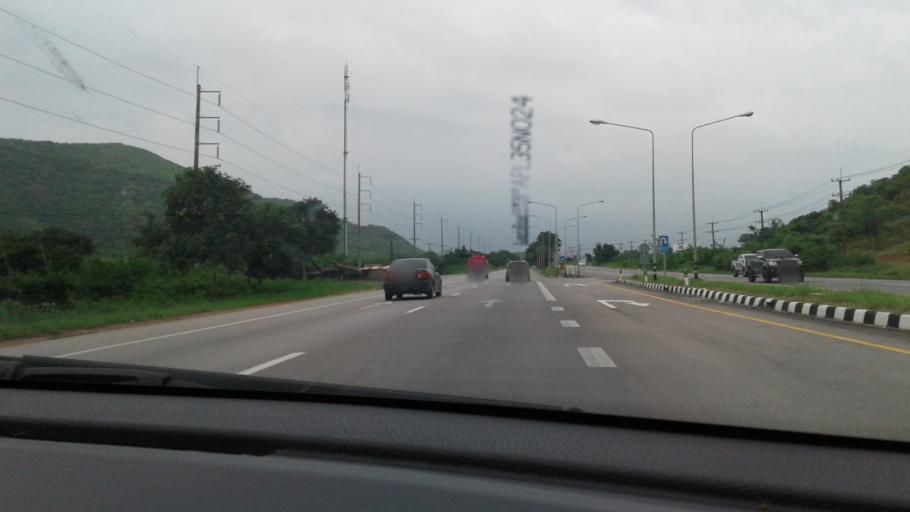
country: TH
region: Prachuap Khiri Khan
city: Prachuap Khiri Khan
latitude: 11.9097
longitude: 99.7974
